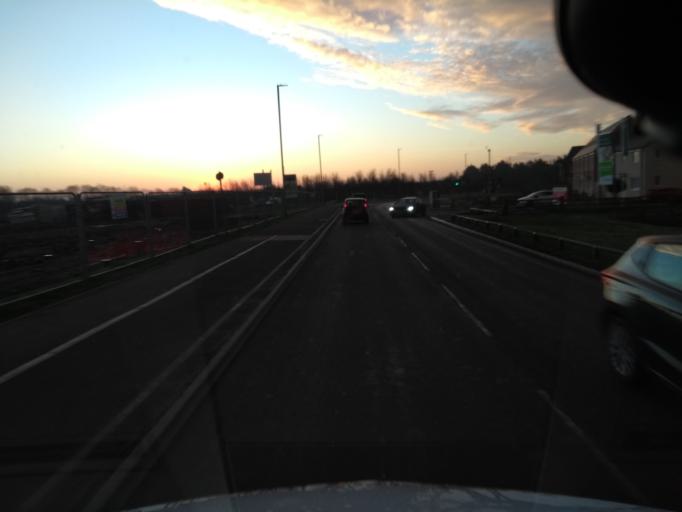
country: GB
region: England
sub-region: Somerset
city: Puriton
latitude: 51.1464
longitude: -2.9804
